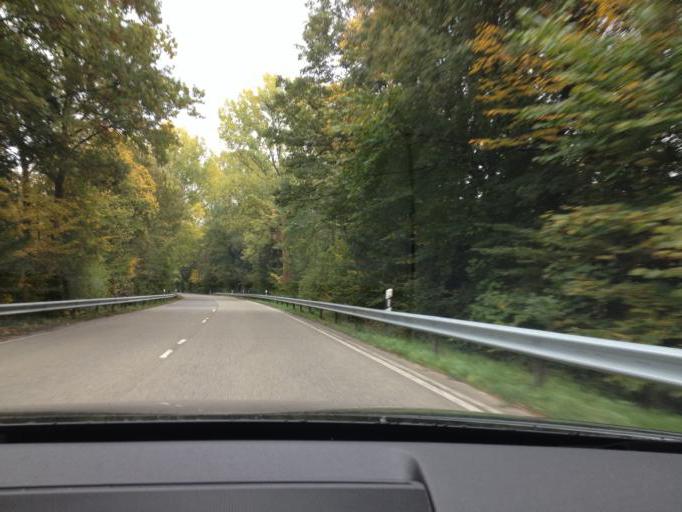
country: DE
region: Rheinland-Pfalz
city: Zweibrucken
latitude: 49.2529
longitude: 7.3900
